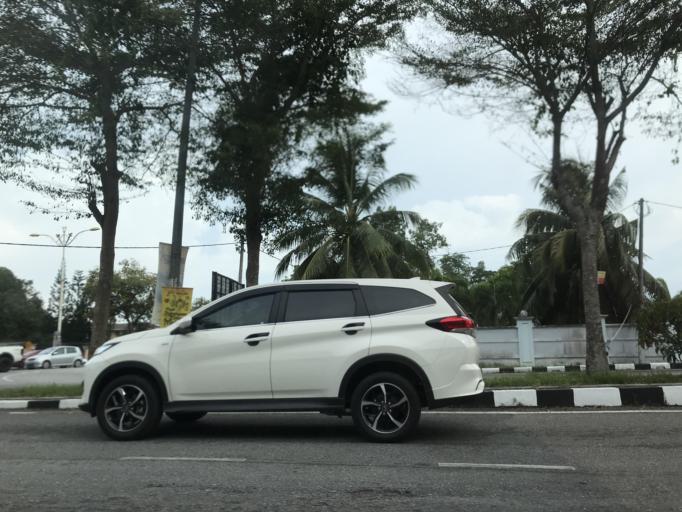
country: MY
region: Kelantan
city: Kota Bharu
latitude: 6.1110
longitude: 102.2374
